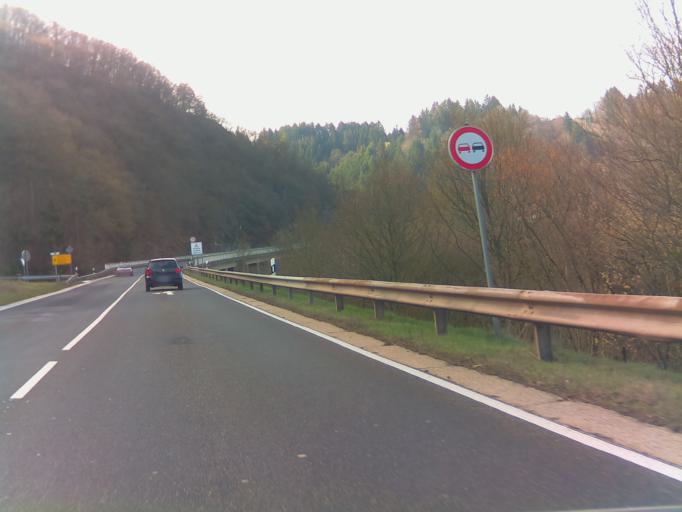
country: DE
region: Rheinland-Pfalz
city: Frauenberg
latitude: 49.6691
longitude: 7.2865
